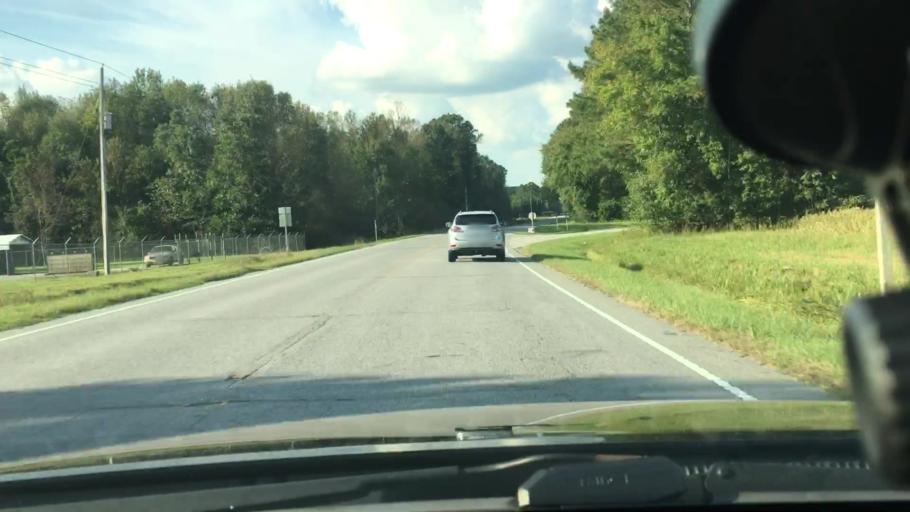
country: US
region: North Carolina
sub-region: Pitt County
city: Windsor
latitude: 35.4343
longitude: -77.2629
